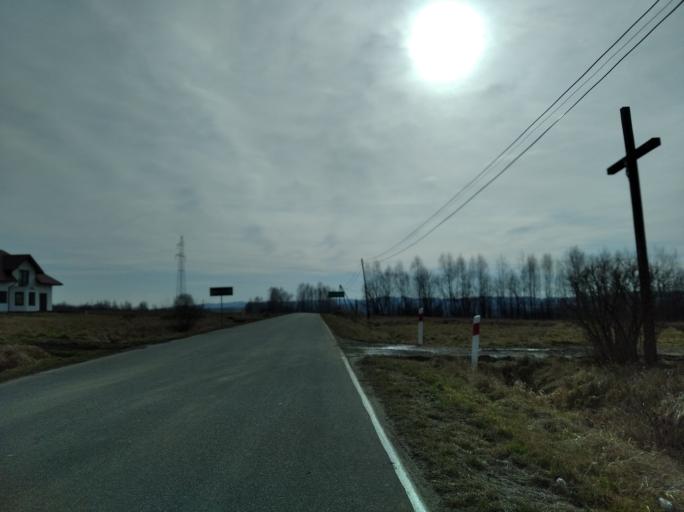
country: PL
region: Subcarpathian Voivodeship
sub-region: Powiat brzozowski
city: Jasienica Rosielna
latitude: 49.7440
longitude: 21.9425
